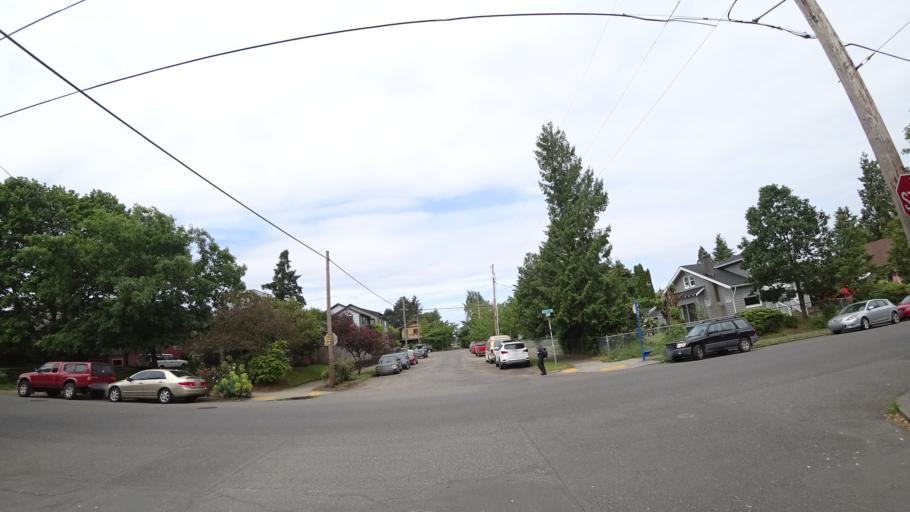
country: US
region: Oregon
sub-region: Multnomah County
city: Portland
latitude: 45.5615
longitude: -122.6347
